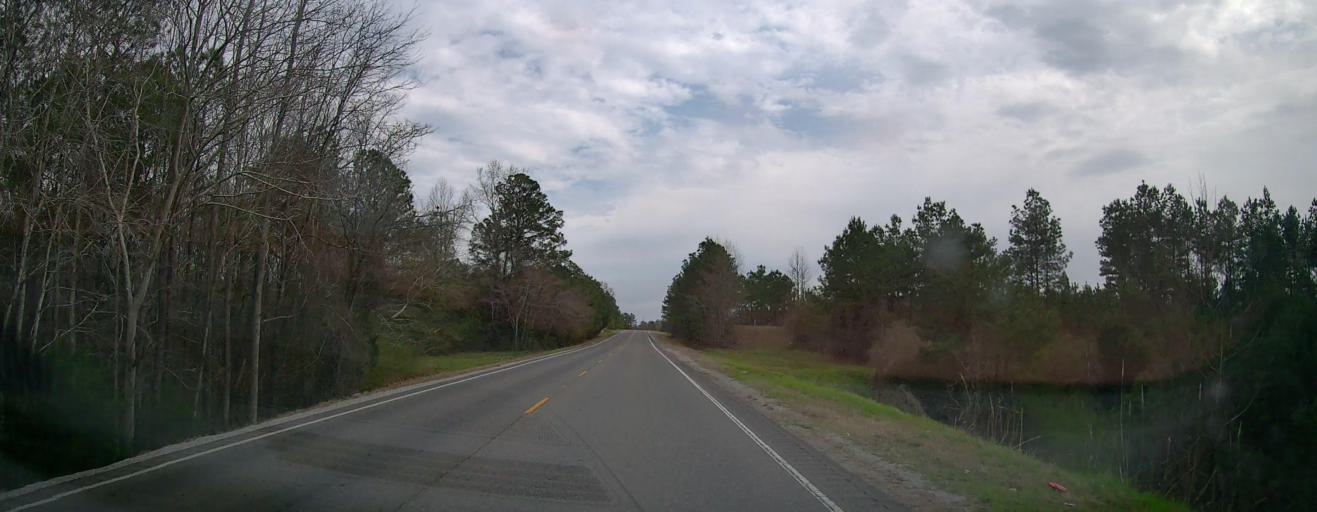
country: US
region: Alabama
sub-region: Marion County
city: Guin
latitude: 34.0419
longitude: -87.9549
